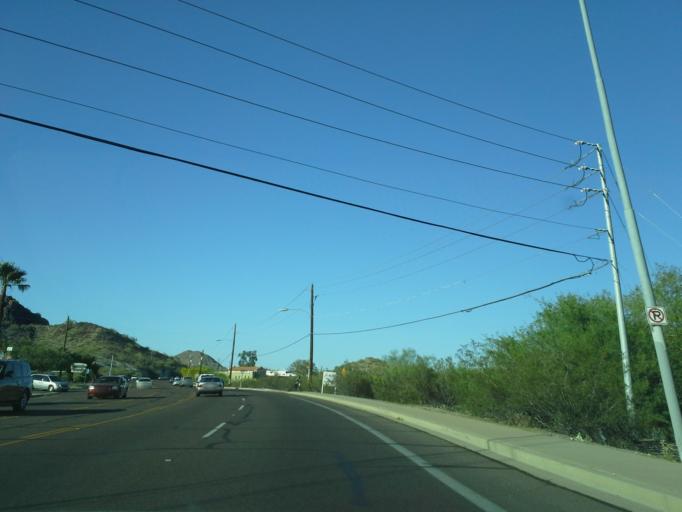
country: US
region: Arizona
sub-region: Maricopa County
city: Paradise Valley
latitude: 33.5906
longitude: -112.0439
